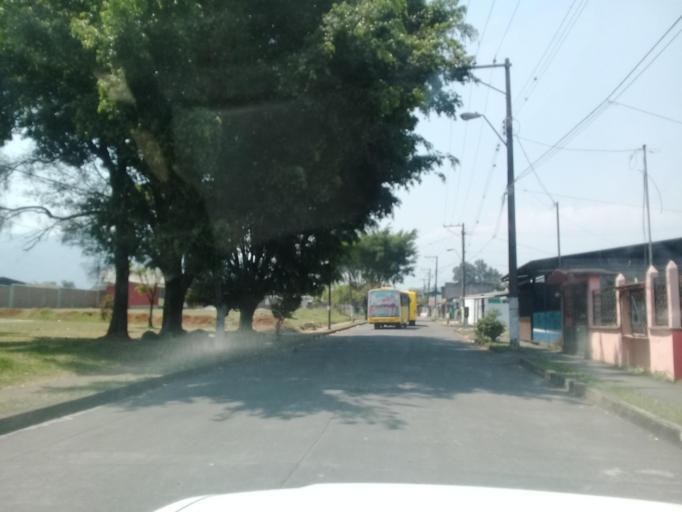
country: MX
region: Veracruz
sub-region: Ixtaczoquitlan
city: Buenavista
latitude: 18.8756
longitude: -97.0496
